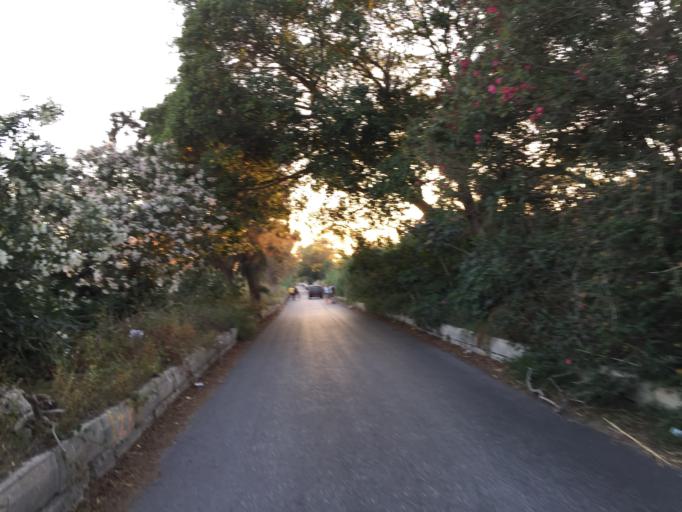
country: MT
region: Il-Marsa
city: Marsa
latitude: 35.8768
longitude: 14.4903
